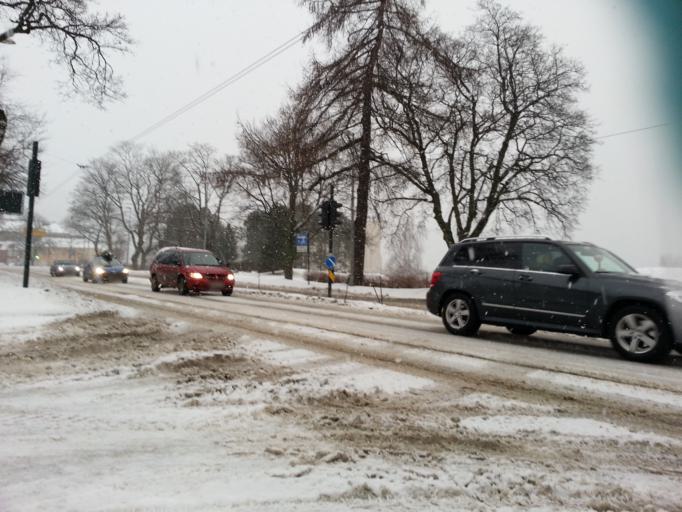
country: NO
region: Sor-Trondelag
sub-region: Trondheim
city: Trondheim
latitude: 63.4302
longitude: 10.3776
